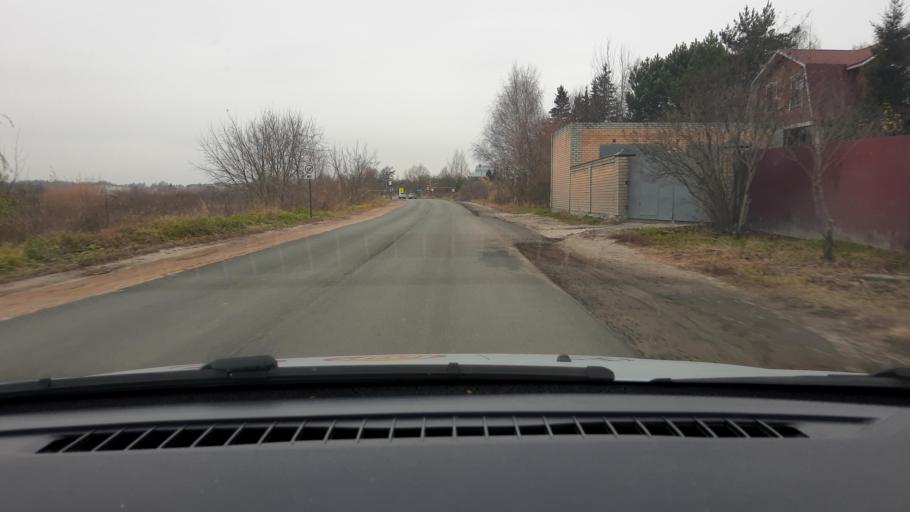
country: RU
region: Nizjnij Novgorod
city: Neklyudovo
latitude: 56.4195
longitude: 43.9650
